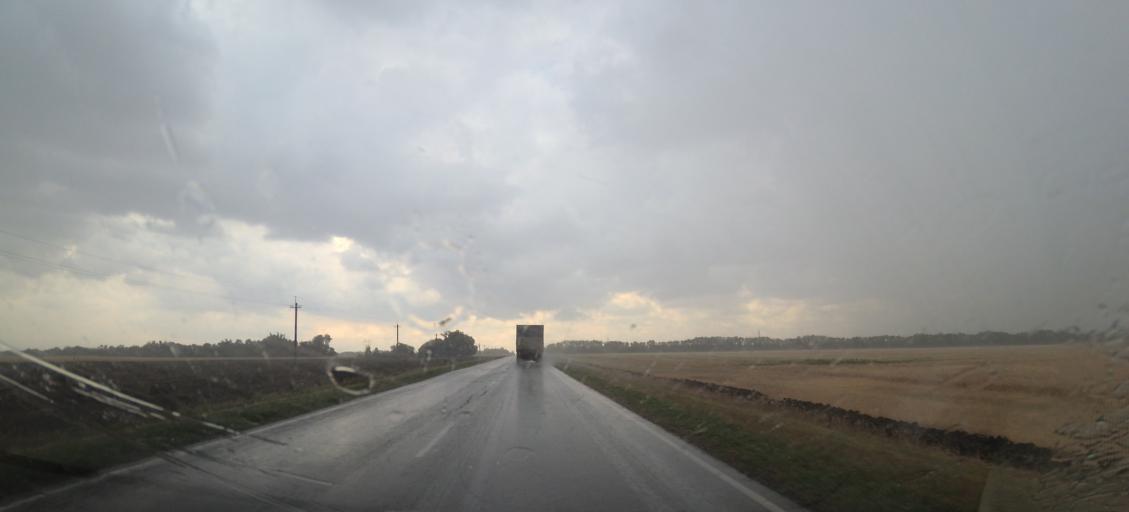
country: RU
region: Rostov
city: Gundorovskiy
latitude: 46.8593
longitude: 41.9435
